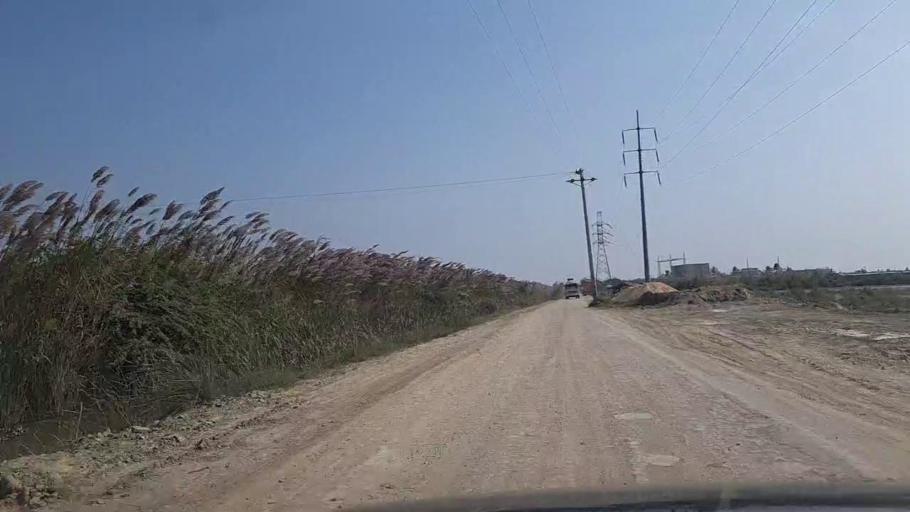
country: PK
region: Sindh
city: Gharo
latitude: 24.7218
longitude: 67.5540
